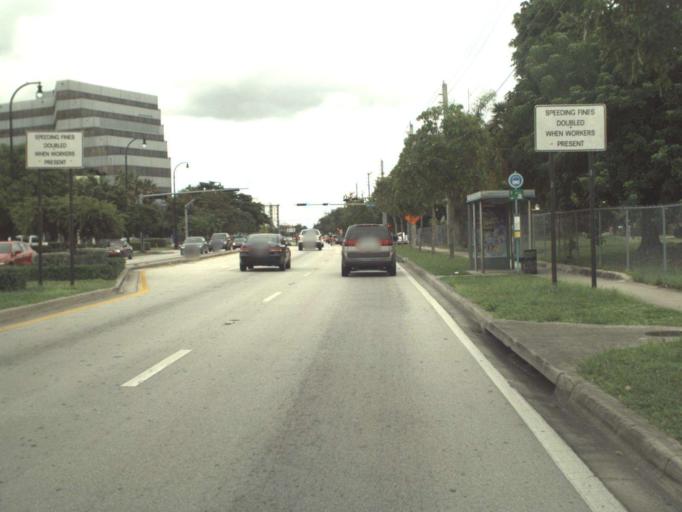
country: US
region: Florida
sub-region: Miami-Dade County
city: Biscayne Park
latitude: 25.8842
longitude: -80.1653
